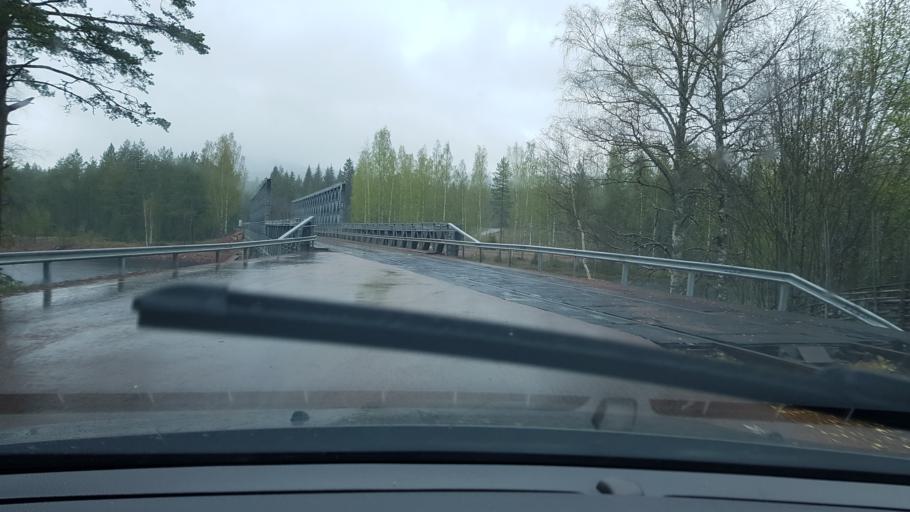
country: SE
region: Dalarna
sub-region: Alvdalens Kommun
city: AElvdalen
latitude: 61.1320
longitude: 14.1718
